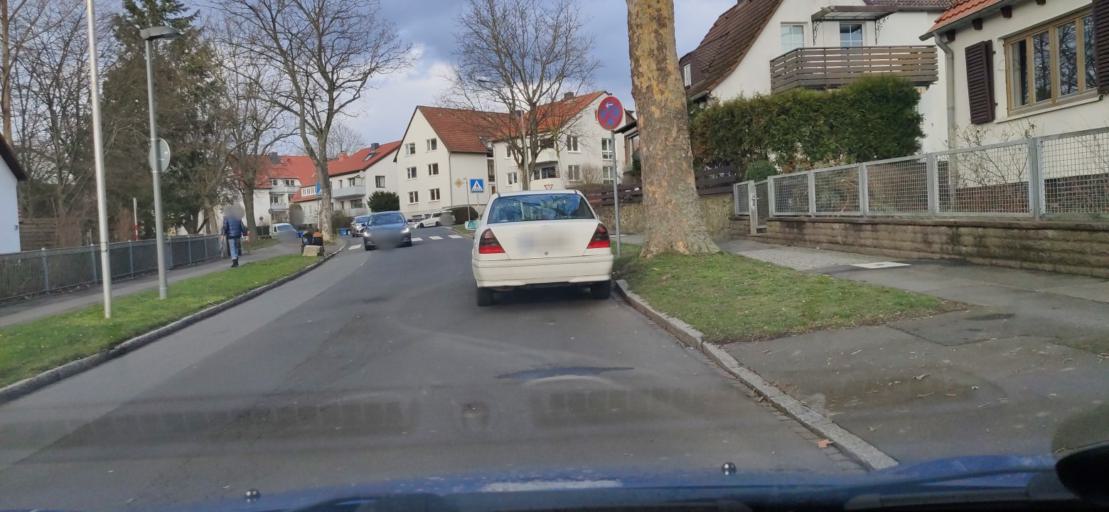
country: DE
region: Lower Saxony
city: Goettingen
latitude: 51.5240
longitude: 9.9550
